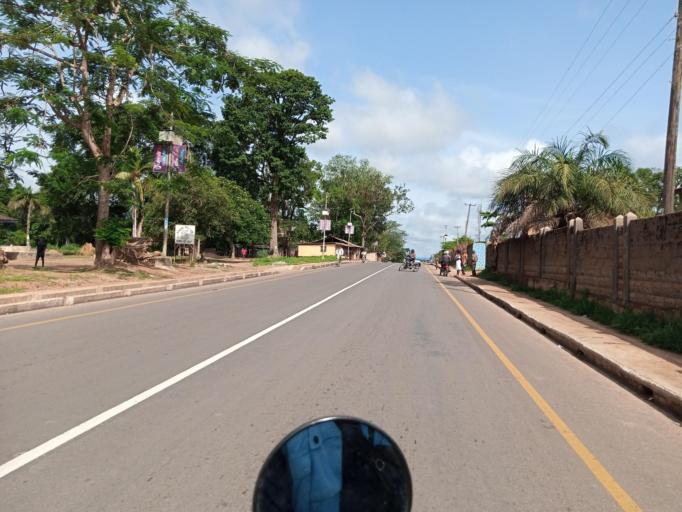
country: SL
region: Southern Province
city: Bo
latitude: 7.9569
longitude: -11.7271
